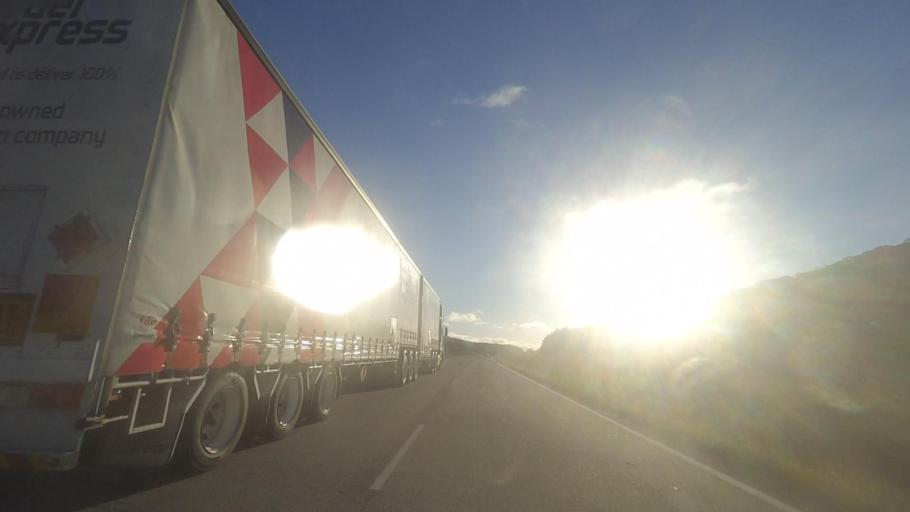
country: AU
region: New South Wales
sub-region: Great Lakes
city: Bulahdelah
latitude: -32.5202
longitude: 152.2044
